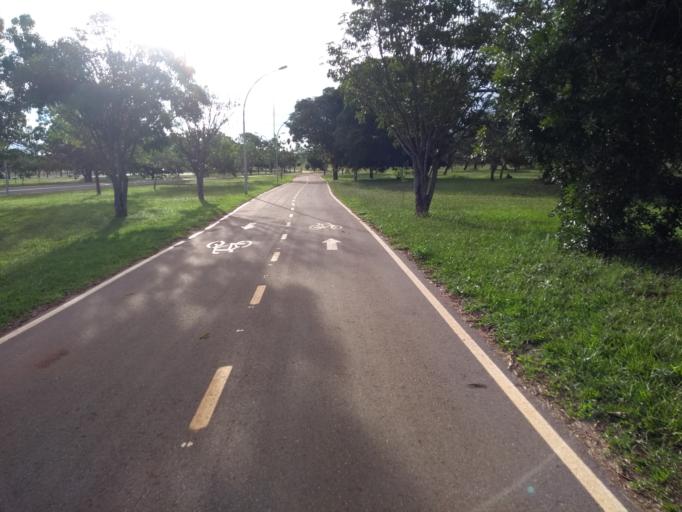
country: BR
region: Federal District
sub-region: Brasilia
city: Brasilia
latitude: -15.8093
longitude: -47.9172
